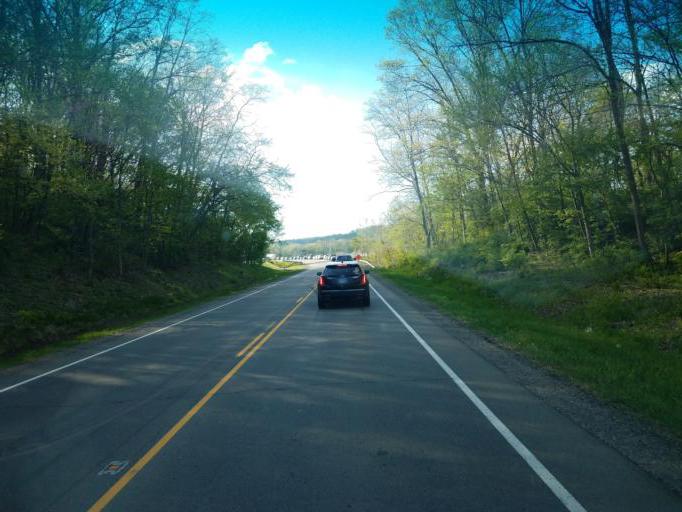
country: US
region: Ohio
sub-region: Coshocton County
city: Coshocton
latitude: 40.3002
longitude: -81.8946
